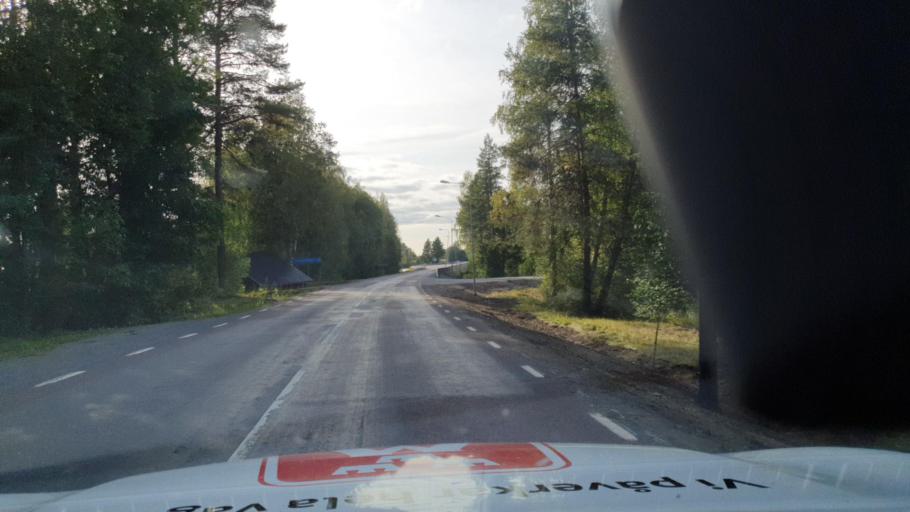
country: SE
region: Jaemtland
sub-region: Stroemsunds Kommun
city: Stroemsund
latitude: 63.7195
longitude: 15.8299
